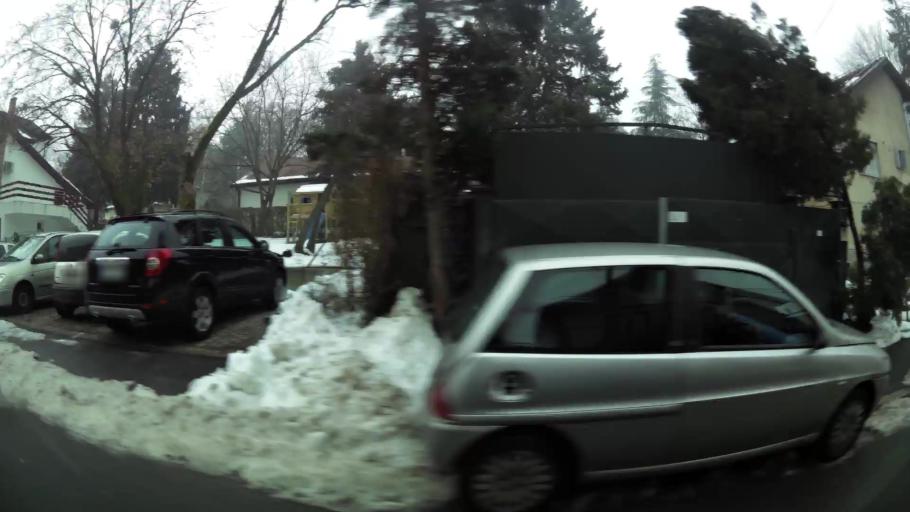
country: RS
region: Central Serbia
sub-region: Belgrade
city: Savski Venac
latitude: 44.7788
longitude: 20.4646
